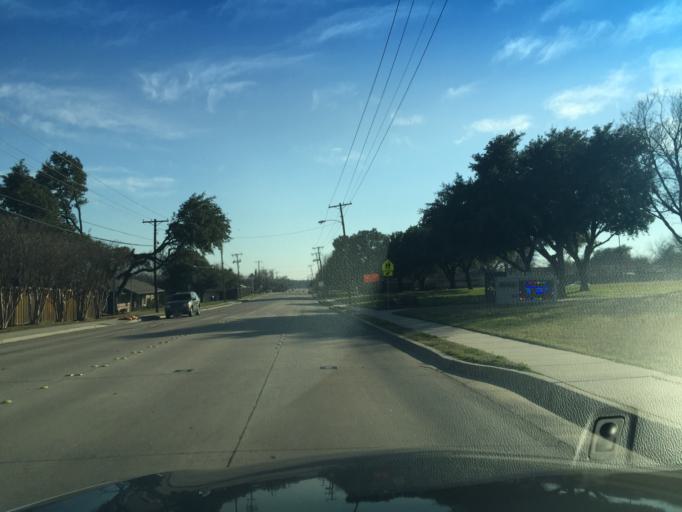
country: US
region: Texas
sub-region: Dallas County
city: Carrollton
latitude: 32.9838
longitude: -96.8840
